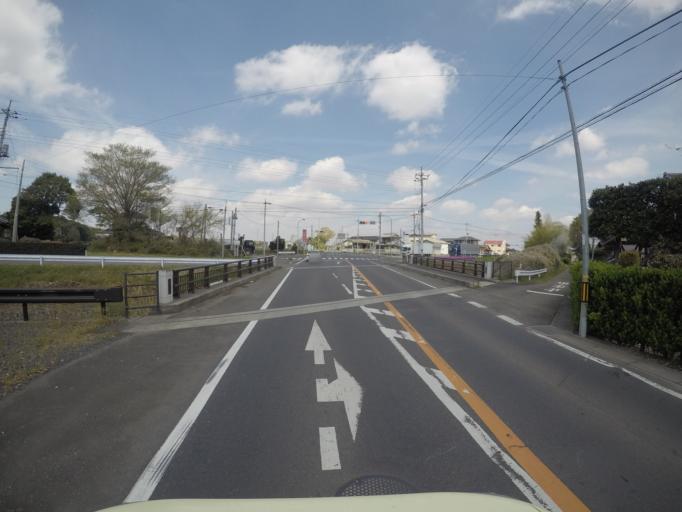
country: JP
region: Ibaraki
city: Shimodate
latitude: 36.2562
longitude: 140.0307
